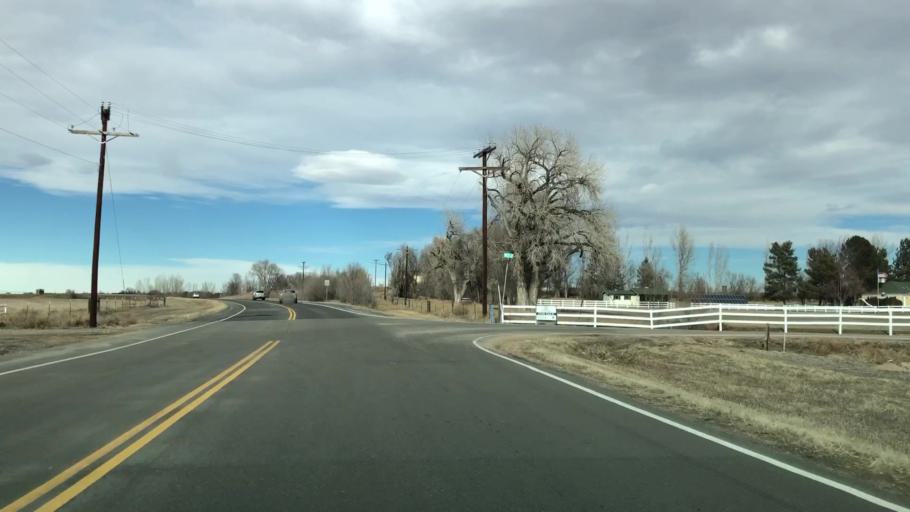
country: US
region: Colorado
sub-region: Weld County
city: Windsor
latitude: 40.5083
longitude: -104.9266
